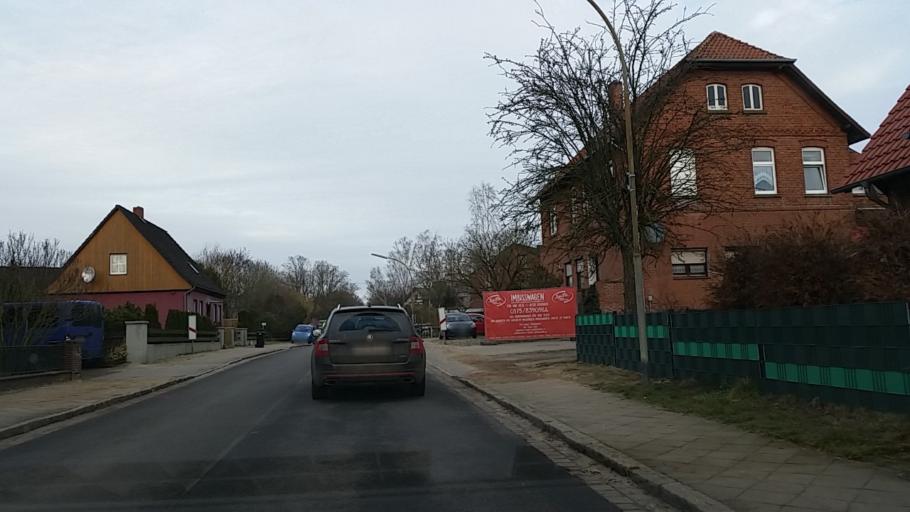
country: DE
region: Lower Saxony
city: Soltendieck
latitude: 52.8733
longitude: 10.7610
